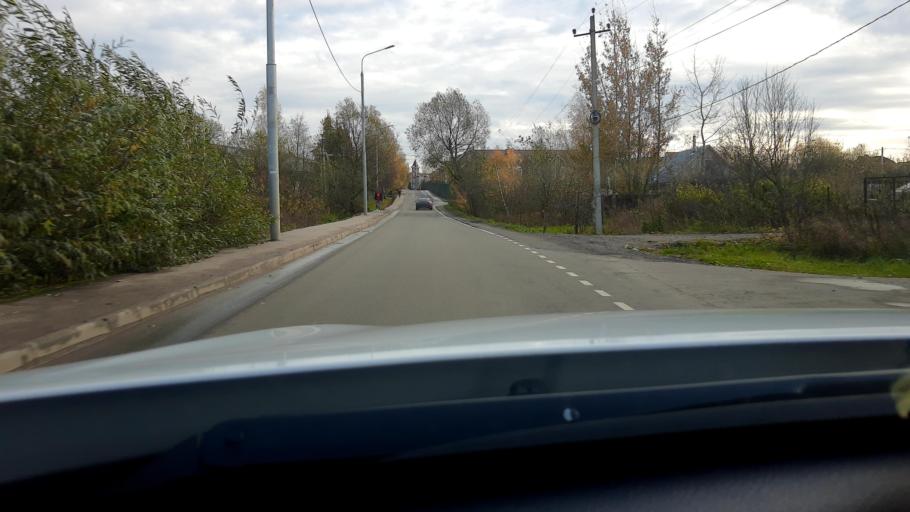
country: RU
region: Moskovskaya
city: Kokoshkino
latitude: 55.5288
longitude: 37.1547
